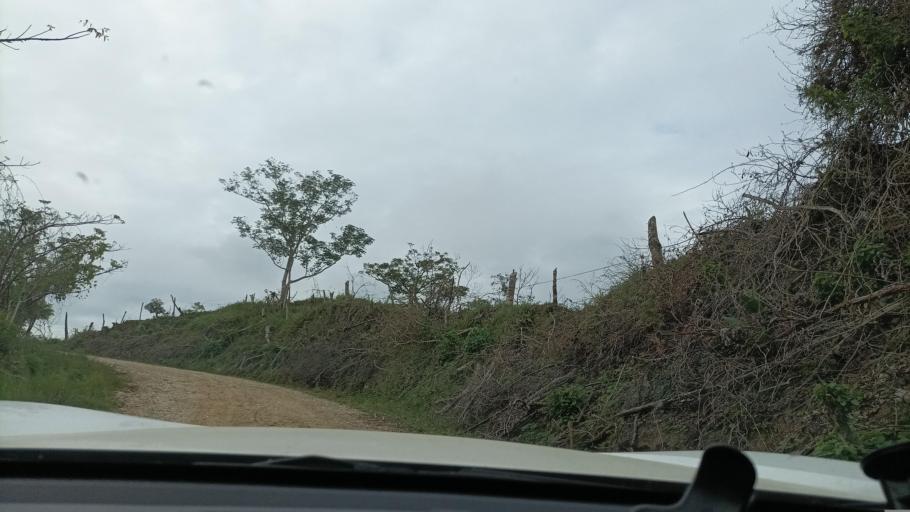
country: MX
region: Veracruz
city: Hidalgotitlan
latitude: 17.5833
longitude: -94.4229
